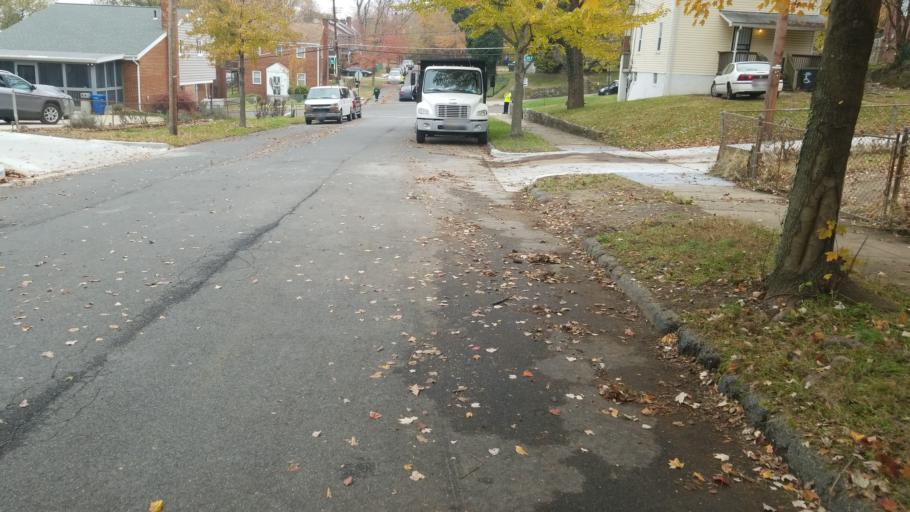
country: US
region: Maryland
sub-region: Prince George's County
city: Coral Hills
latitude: 38.8749
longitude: -76.9346
